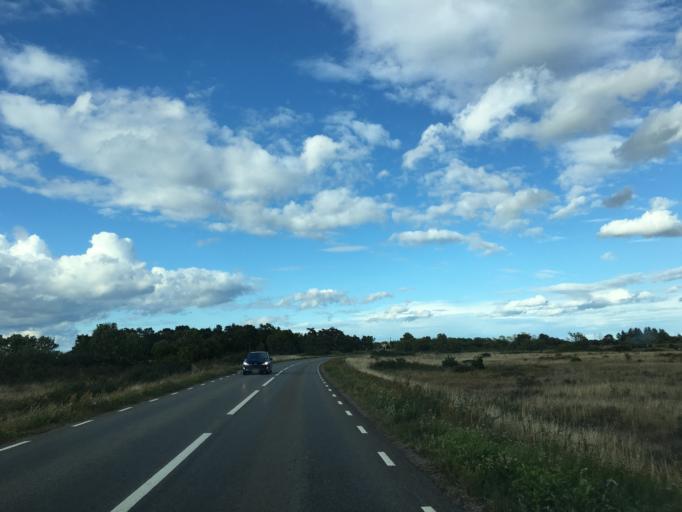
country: SE
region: Kalmar
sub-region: Morbylanga Kommun
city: Moerbylanga
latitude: 56.5028
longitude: 16.4306
